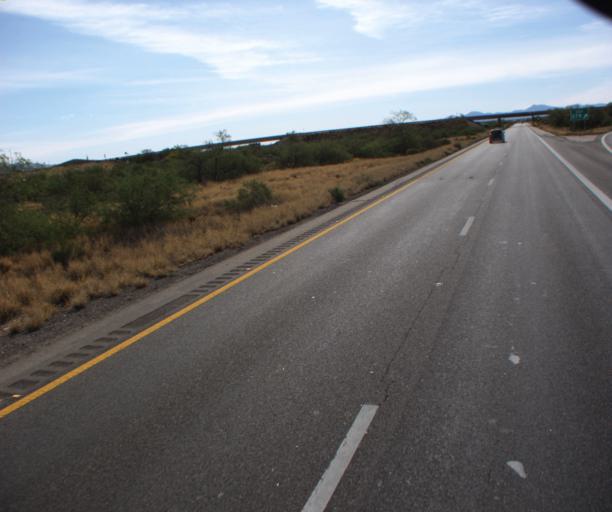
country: US
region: Arizona
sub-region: Pima County
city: Vail
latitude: 32.0289
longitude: -110.7235
